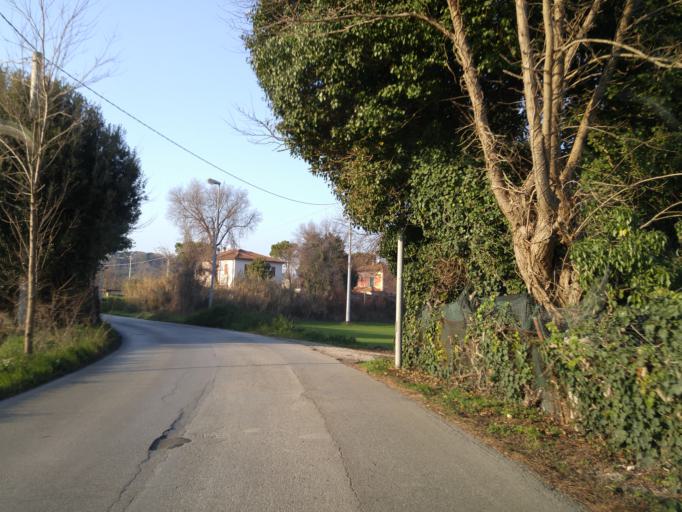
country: IT
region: The Marches
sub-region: Provincia di Pesaro e Urbino
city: Centinarola
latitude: 43.8249
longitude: 12.9945
